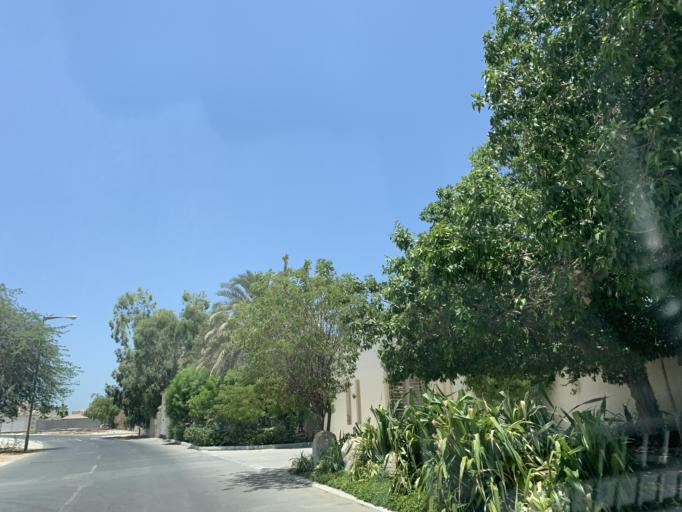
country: BH
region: Manama
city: Jidd Hafs
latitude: 26.2250
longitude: 50.4866
